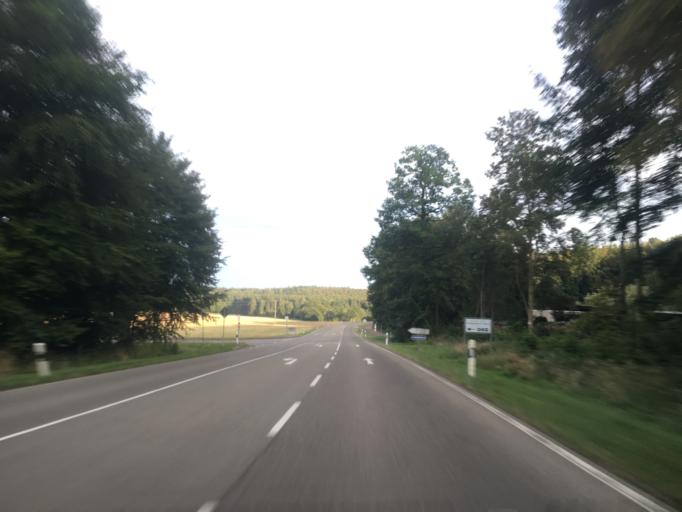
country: DE
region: Baden-Wuerttemberg
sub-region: Tuebingen Region
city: Sankt Johann
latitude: 48.4847
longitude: 9.3237
